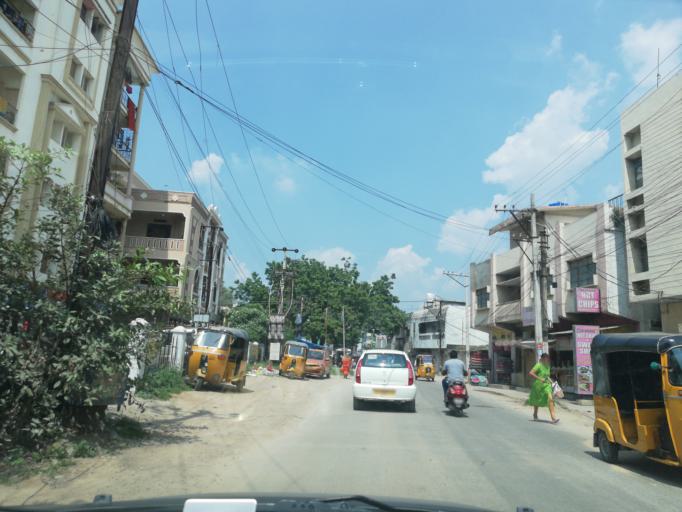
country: IN
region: Telangana
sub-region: Medak
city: Serilingampalle
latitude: 17.4902
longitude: 78.3186
